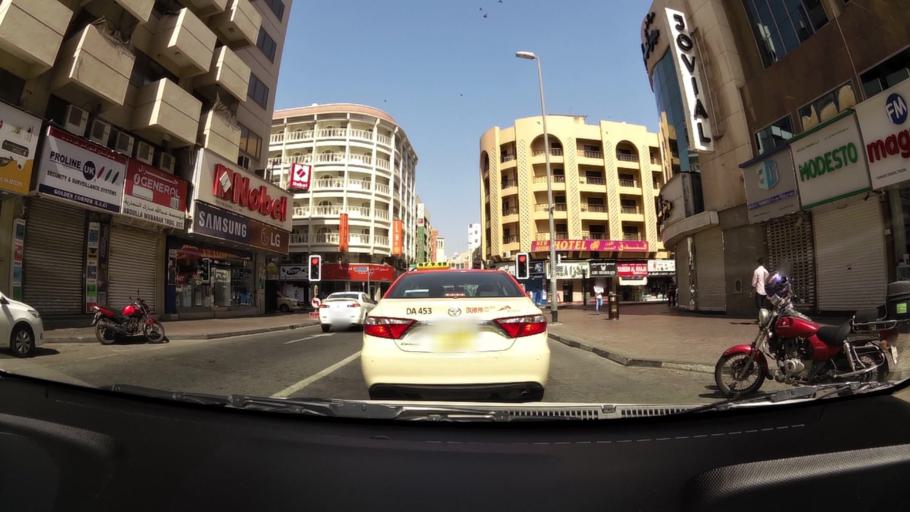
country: AE
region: Ash Shariqah
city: Sharjah
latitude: 25.2689
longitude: 55.3037
